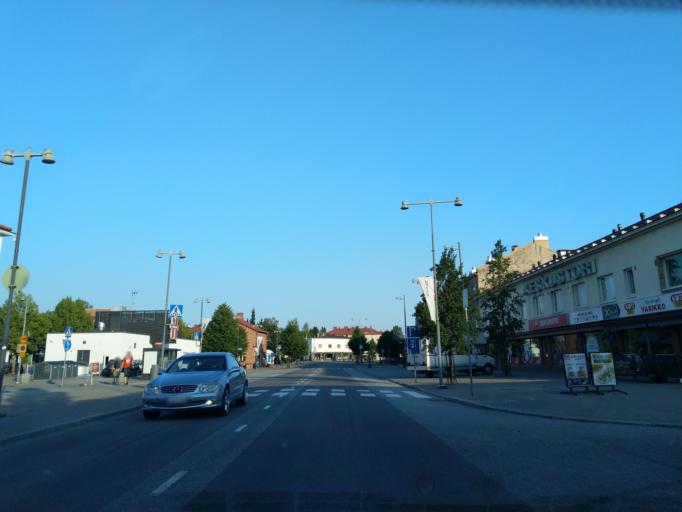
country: FI
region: Satakunta
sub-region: Pohjois-Satakunta
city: Kankaanpaeae
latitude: 61.8045
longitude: 22.3931
